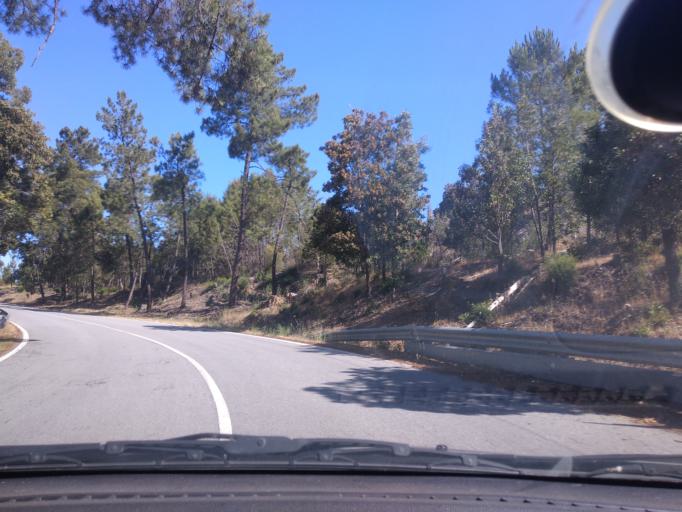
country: PT
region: Portalegre
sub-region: Nisa
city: Nisa
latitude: 39.6047
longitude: -7.6605
